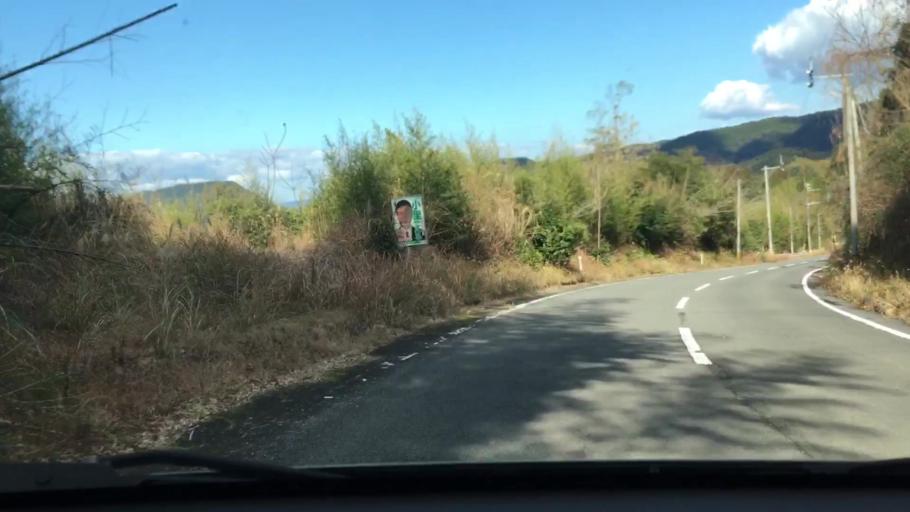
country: JP
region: Kagoshima
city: Ijuin
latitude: 31.7231
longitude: 130.4163
